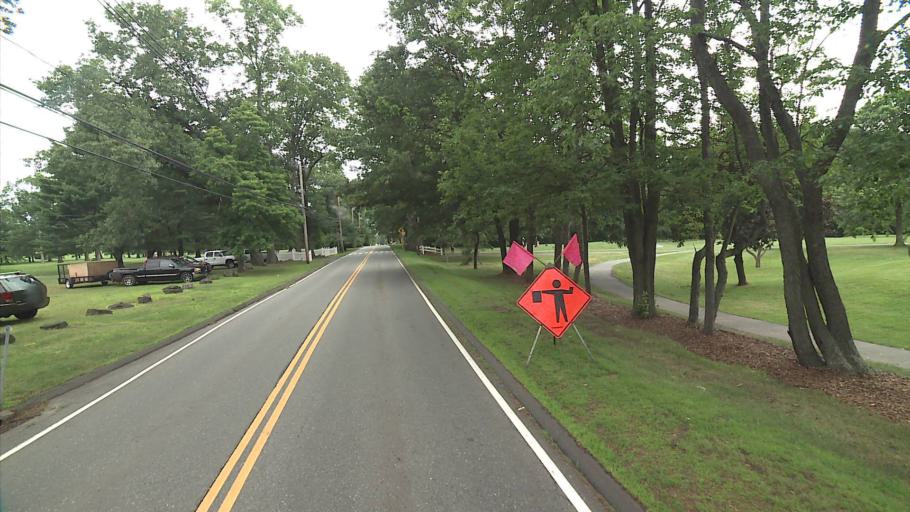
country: US
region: Connecticut
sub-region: New Haven County
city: Wallingford Center
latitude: 41.4412
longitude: -72.8047
